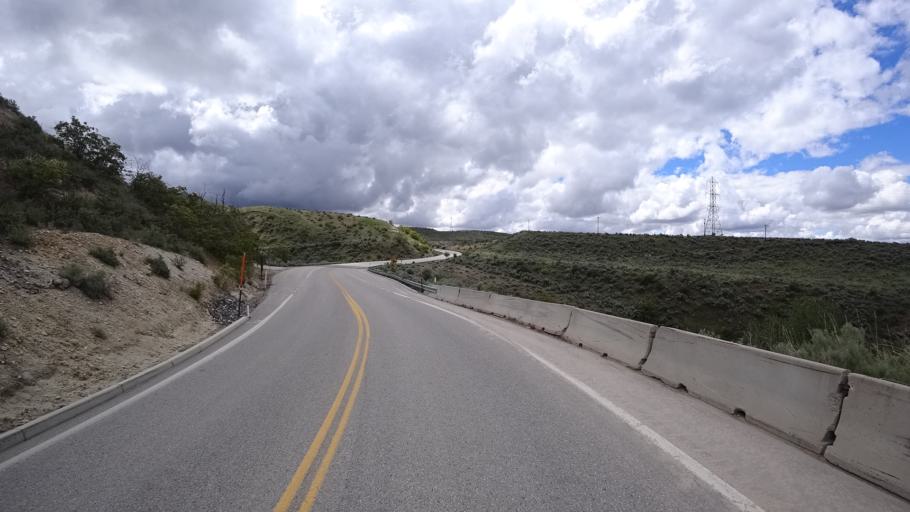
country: US
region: Idaho
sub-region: Ada County
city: Boise
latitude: 43.6778
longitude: -116.1844
